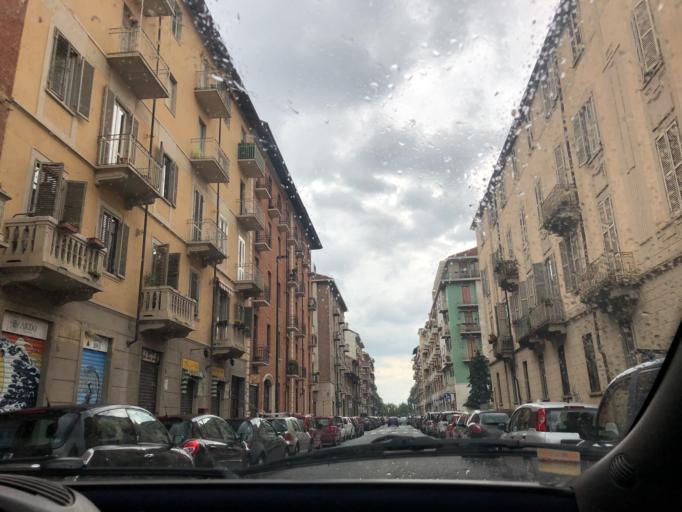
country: IT
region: Piedmont
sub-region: Provincia di Torino
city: Lesna
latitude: 45.0812
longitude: 7.6450
